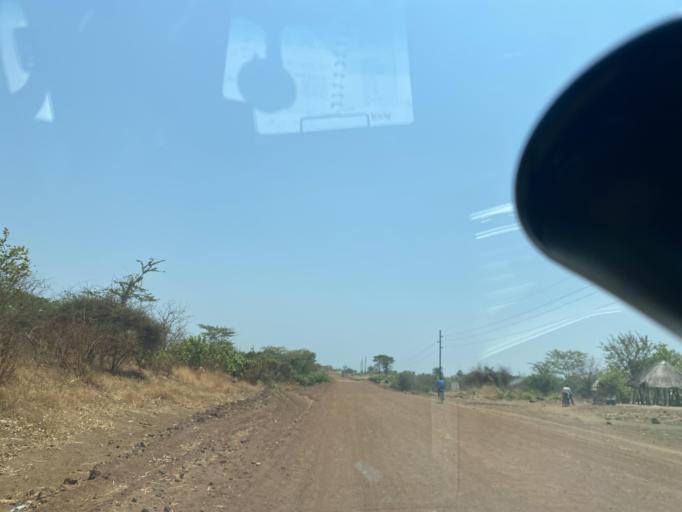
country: ZM
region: Southern
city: Nakambala
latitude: -15.4800
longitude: 27.8988
